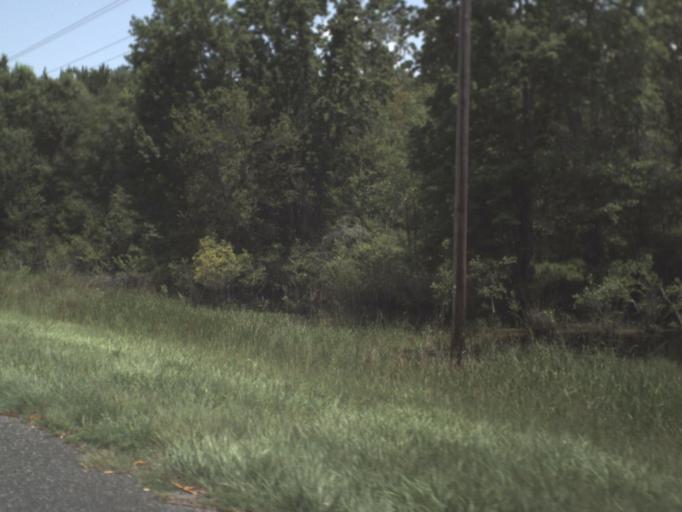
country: US
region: Florida
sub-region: Taylor County
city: Perry
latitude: 29.9791
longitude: -83.4882
